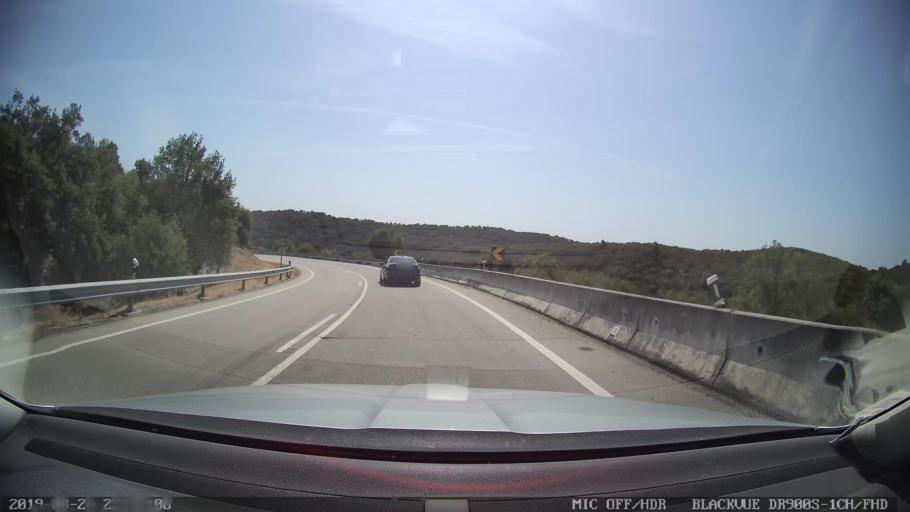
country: PT
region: Castelo Branco
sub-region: Idanha-A-Nova
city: Idanha-a-Nova
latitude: 39.8573
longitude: -7.3425
